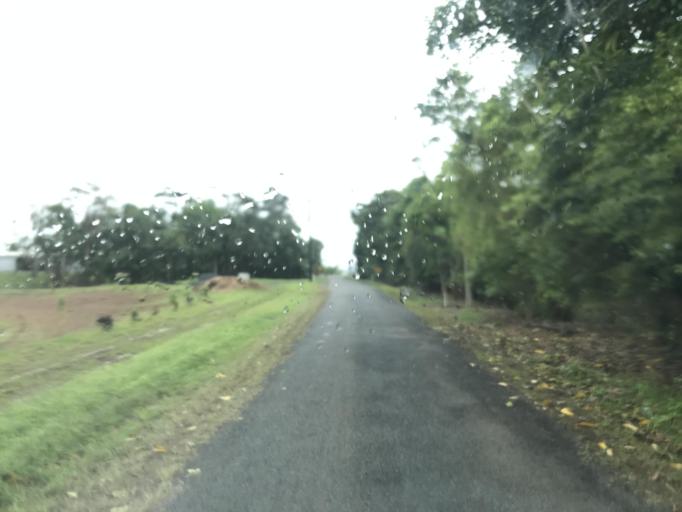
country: AU
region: Queensland
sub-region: Cassowary Coast
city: Innisfail
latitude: -17.4860
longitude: 145.9890
